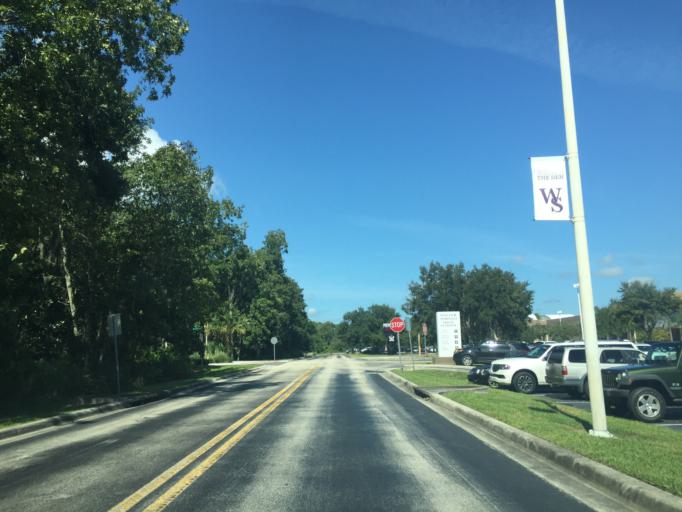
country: US
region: Florida
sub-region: Seminole County
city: Winter Springs
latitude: 28.7023
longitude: -81.2635
